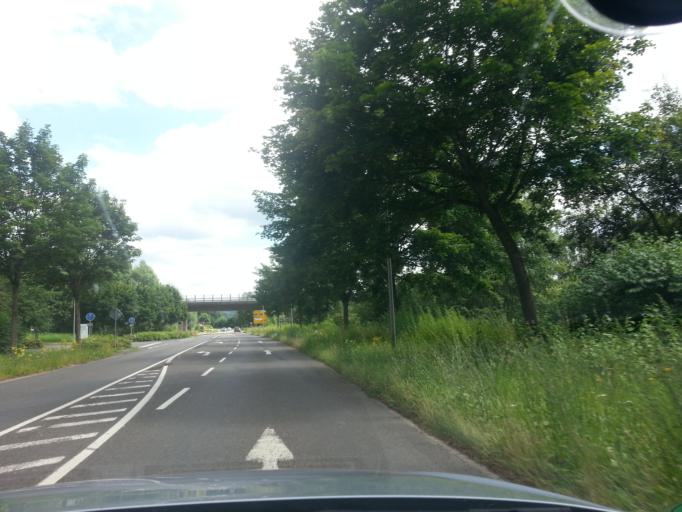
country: DE
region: Saarland
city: Merzig
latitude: 49.4663
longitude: 6.6175
